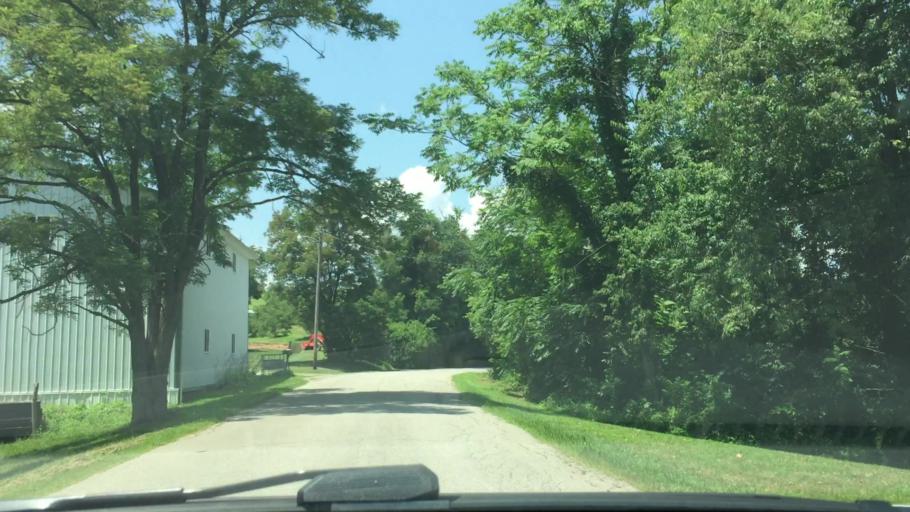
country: US
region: West Virginia
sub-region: Wetzel County
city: New Martinsville
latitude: 39.7114
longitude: -80.7479
